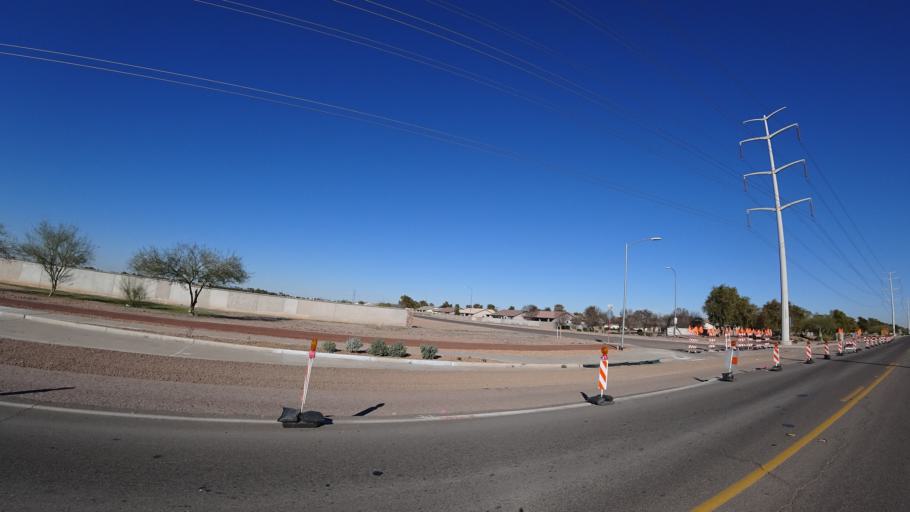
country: US
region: Arizona
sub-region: Maricopa County
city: Tolleson
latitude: 33.4084
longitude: -112.2303
